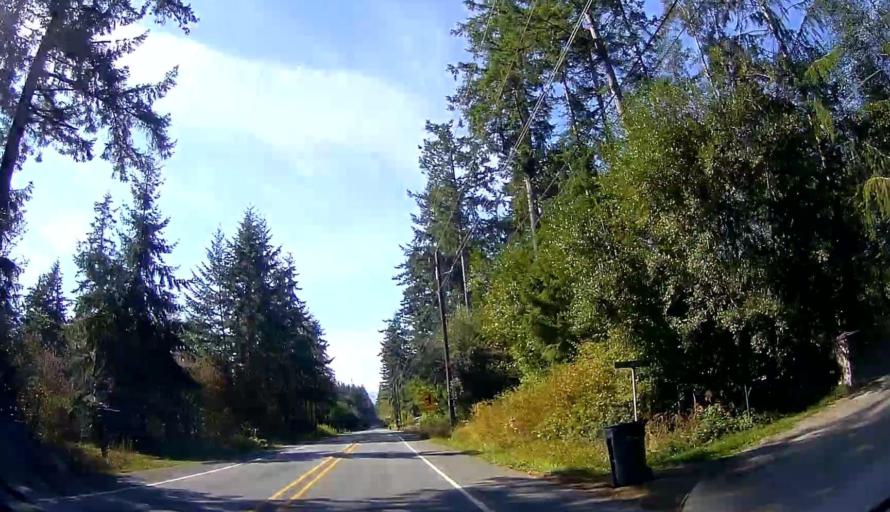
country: US
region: Washington
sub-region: Island County
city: Camano
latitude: 48.2257
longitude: -122.5061
